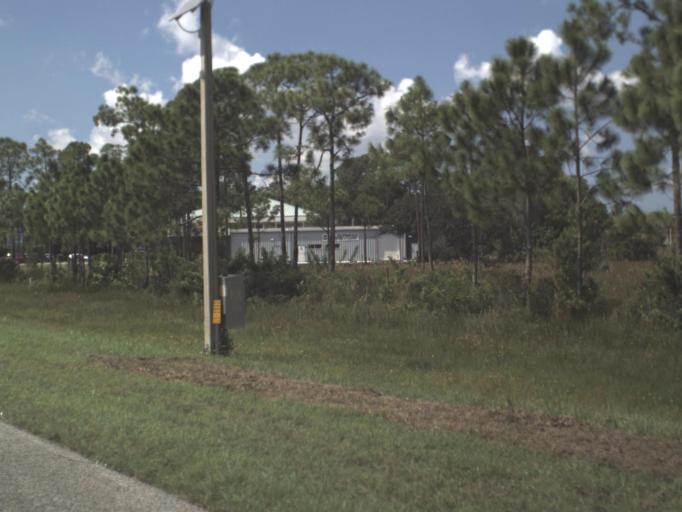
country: US
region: Florida
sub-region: Lee County
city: Fort Myers
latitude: 26.6057
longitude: -81.8263
